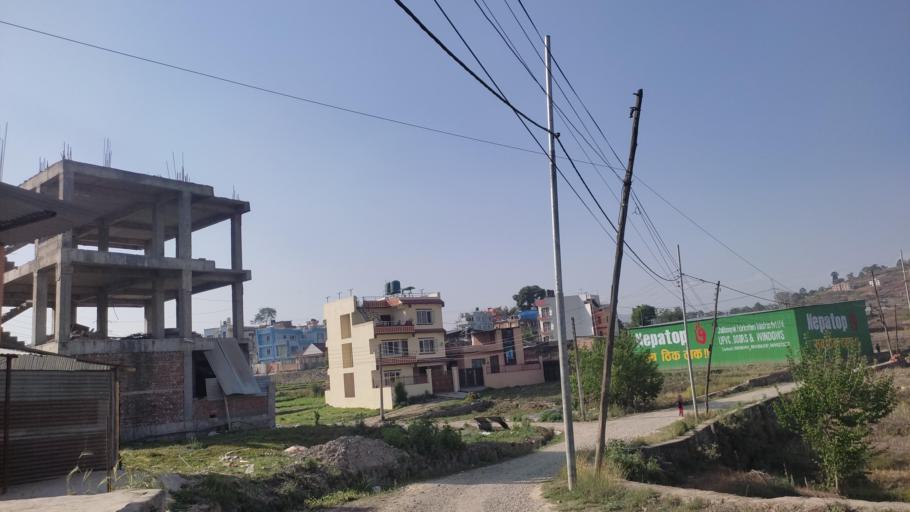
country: NP
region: Central Region
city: Kirtipur
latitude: 27.6552
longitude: 85.2856
